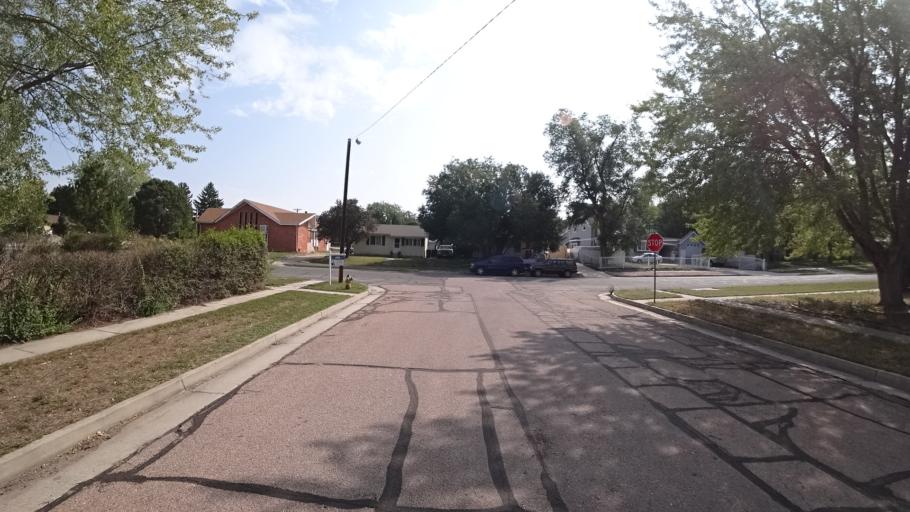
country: US
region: Colorado
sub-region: El Paso County
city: Colorado Springs
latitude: 38.8524
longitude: -104.7847
